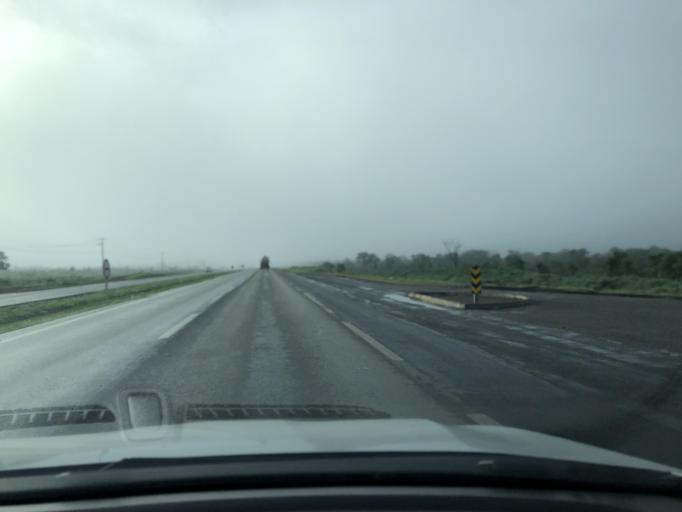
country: BR
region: Goias
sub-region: Luziania
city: Luziania
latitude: -16.2826
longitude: -47.8582
